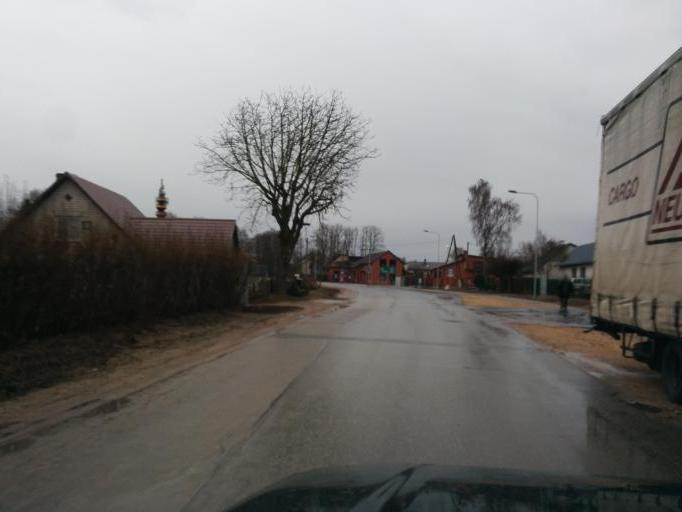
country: LV
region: Kekava
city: Balozi
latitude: 56.8763
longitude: 24.1779
